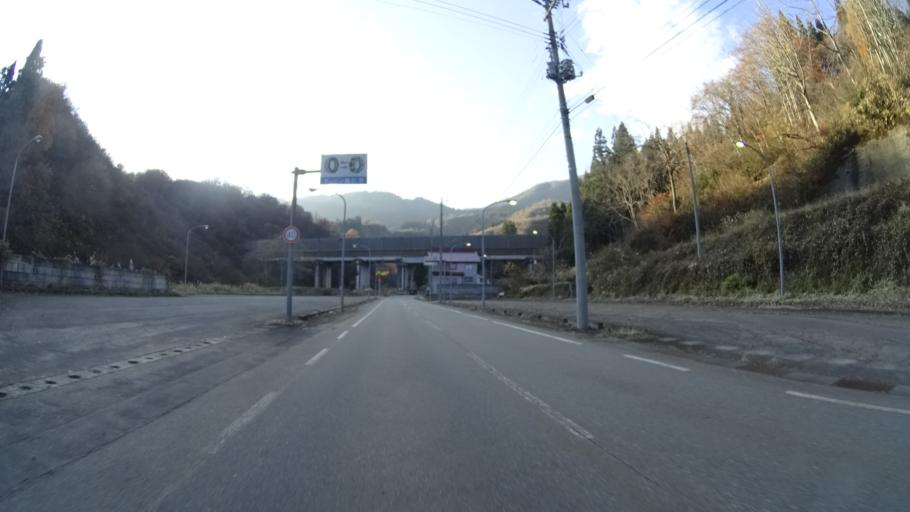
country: JP
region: Niigata
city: Shiozawa
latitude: 36.9873
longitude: 138.7934
